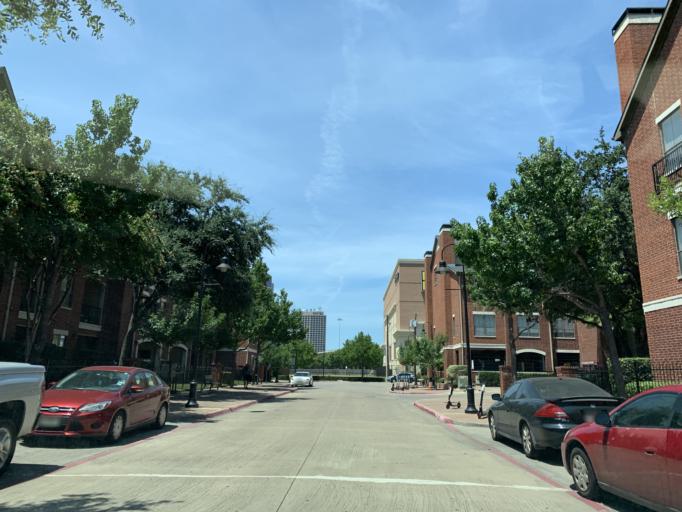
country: US
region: Texas
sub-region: Dallas County
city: Dallas
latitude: 32.7807
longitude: -96.7875
